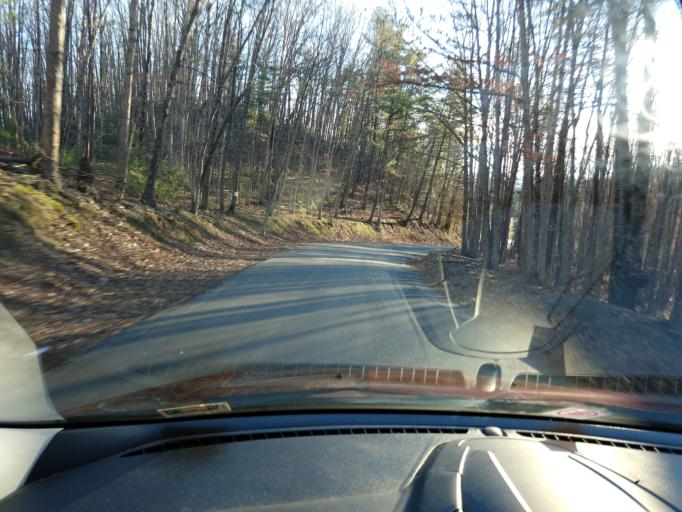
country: US
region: Virginia
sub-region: Alleghany County
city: Clifton Forge
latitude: 37.8441
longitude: -79.8476
